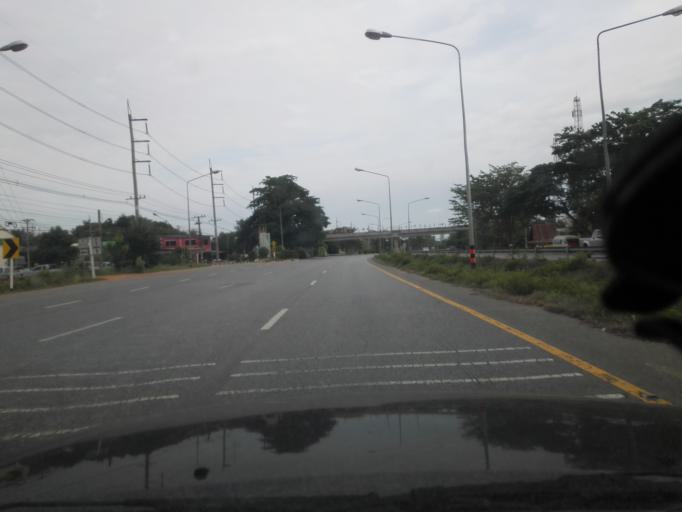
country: TH
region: Kamphaeng Phet
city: Khlong Khlung
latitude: 16.1021
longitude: 99.7197
